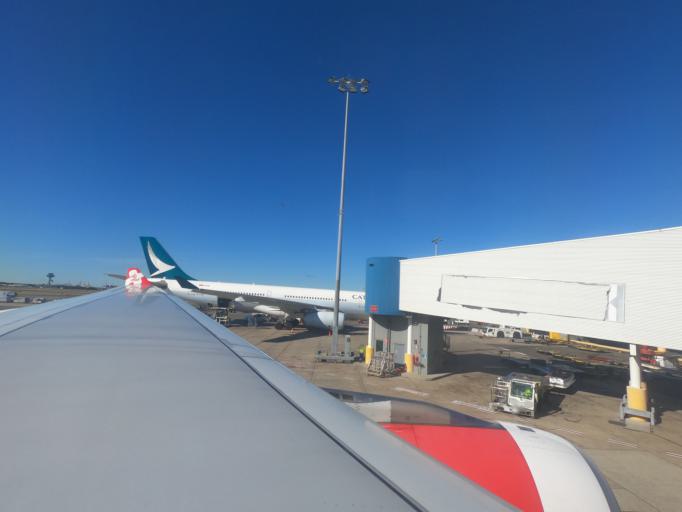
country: AU
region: New South Wales
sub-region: Rockdale
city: Arncliffe
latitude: -33.9387
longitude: 151.1697
